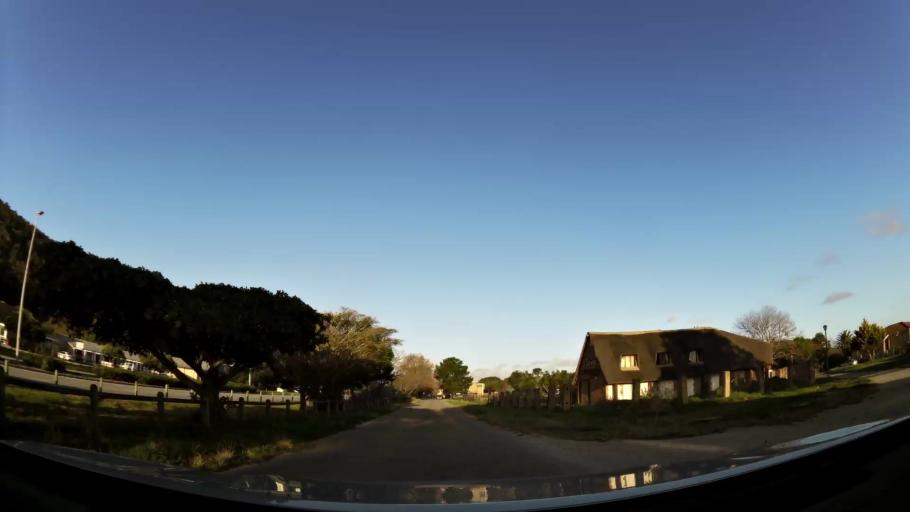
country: ZA
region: Western Cape
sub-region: Eden District Municipality
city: Knysna
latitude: -34.0128
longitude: 22.7982
